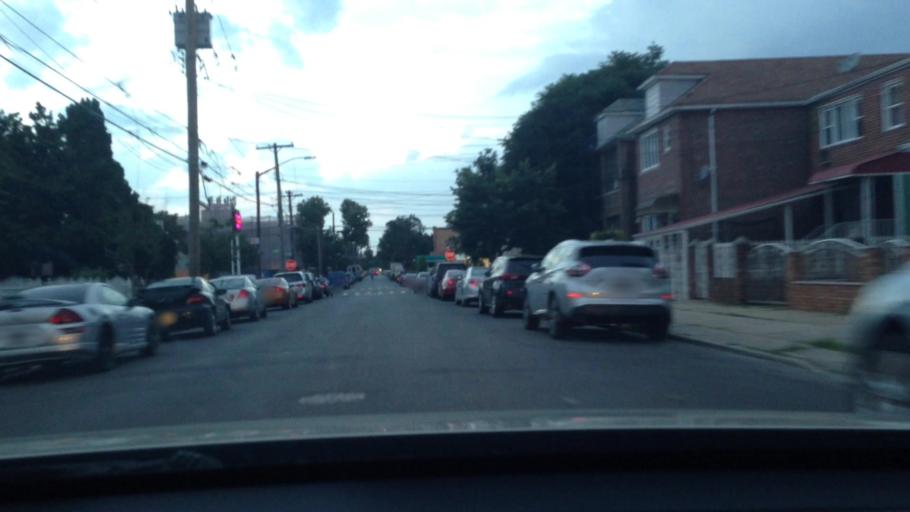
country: US
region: New York
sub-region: Kings County
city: East New York
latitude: 40.6382
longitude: -73.9075
